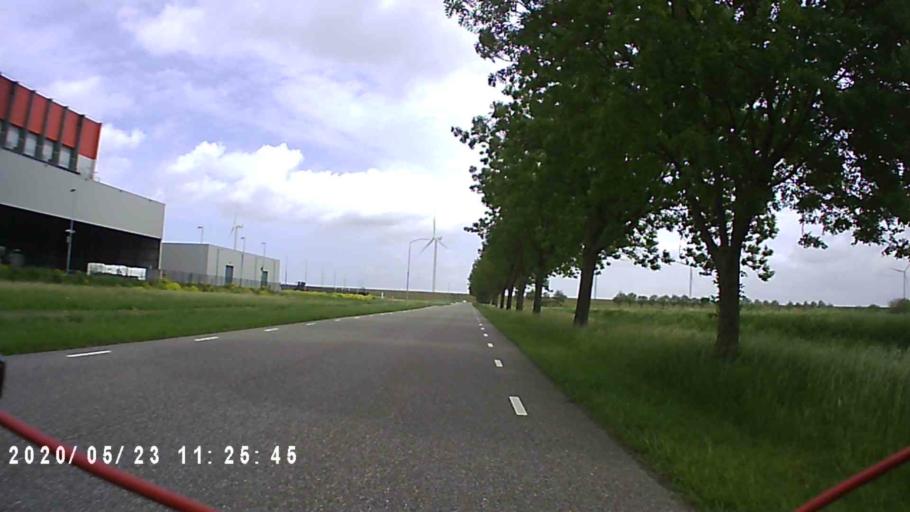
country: NL
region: Groningen
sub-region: Gemeente Delfzijl
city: Delfzijl
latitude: 53.3083
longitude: 6.9901
